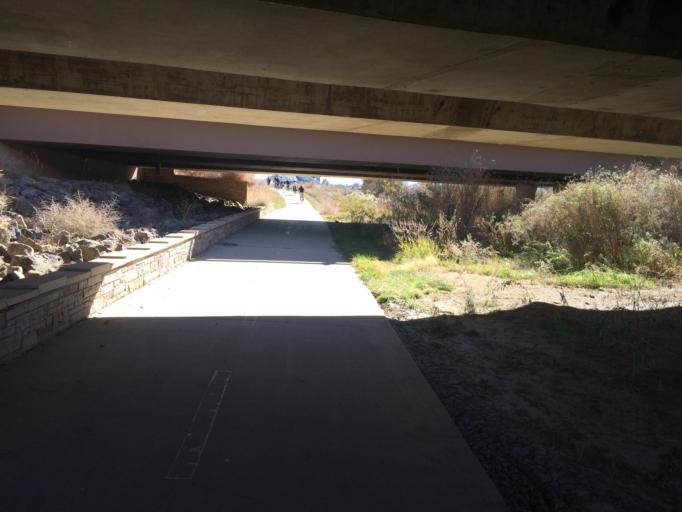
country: US
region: Colorado
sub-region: Boulder County
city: Longmont
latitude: 40.1526
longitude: -105.0901
